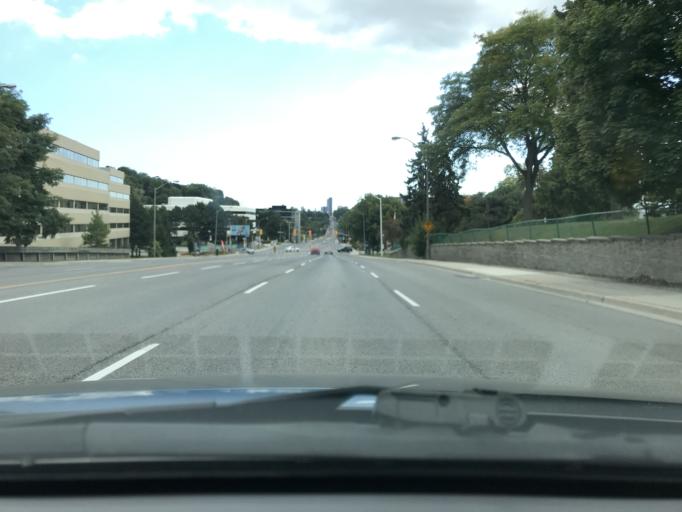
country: CA
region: Ontario
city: North York
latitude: 43.7488
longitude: -79.4079
